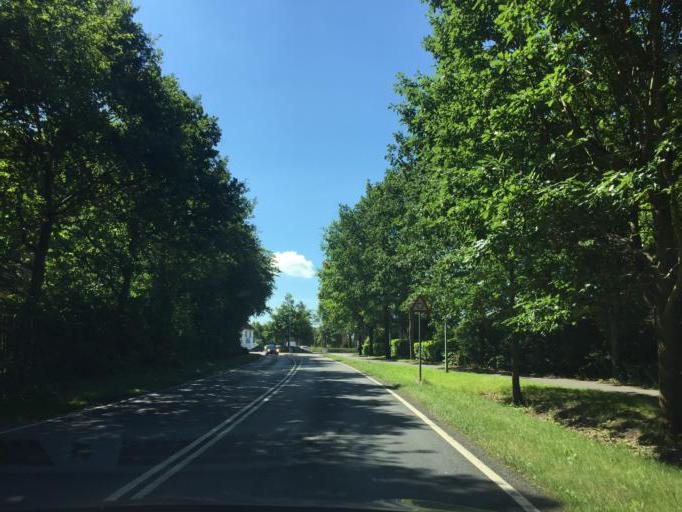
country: DK
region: South Denmark
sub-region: Odense Kommune
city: Bellinge
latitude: 55.3701
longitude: 10.3278
